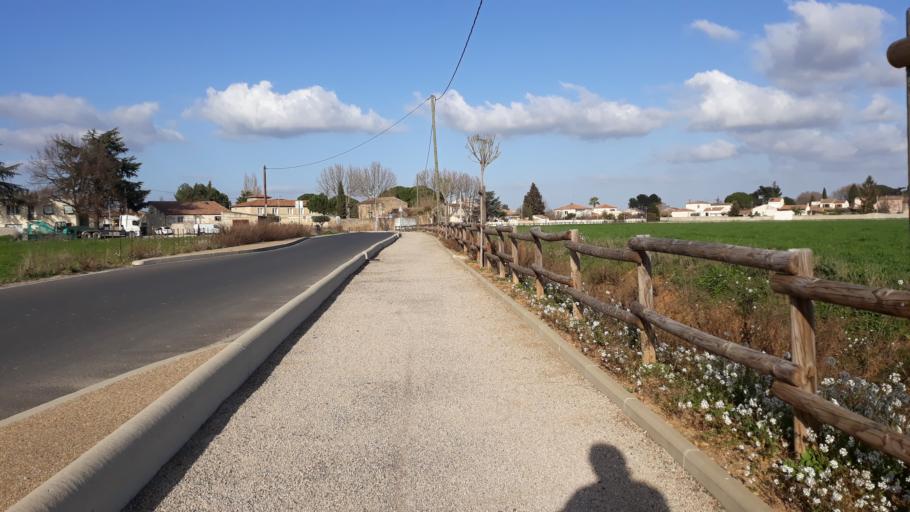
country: FR
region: Languedoc-Roussillon
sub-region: Departement du Gard
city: Aimargues
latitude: 43.6888
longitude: 4.2003
